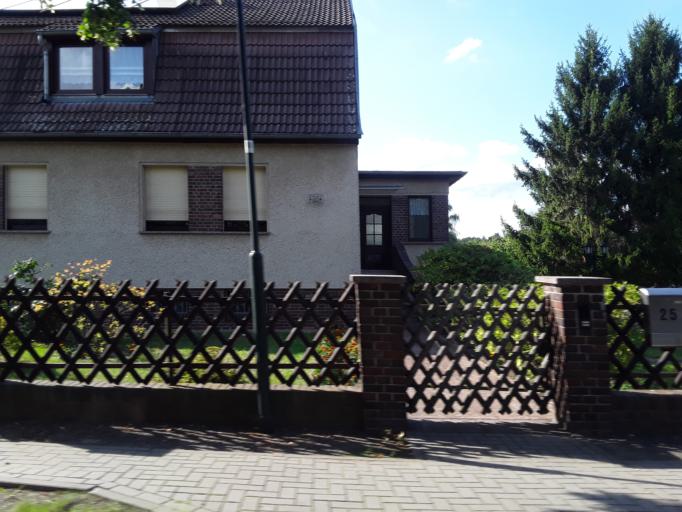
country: DE
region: Berlin
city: Buch
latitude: 52.6256
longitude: 13.5156
